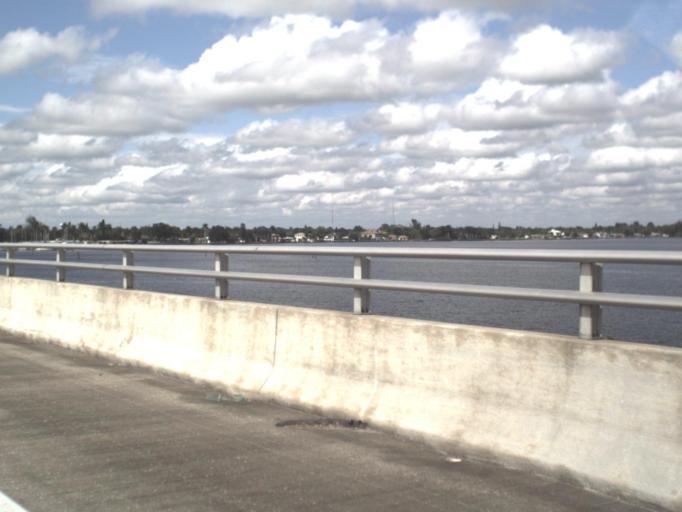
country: US
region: Florida
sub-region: Lee County
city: North Fort Myers
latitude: 26.6577
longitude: -81.8729
